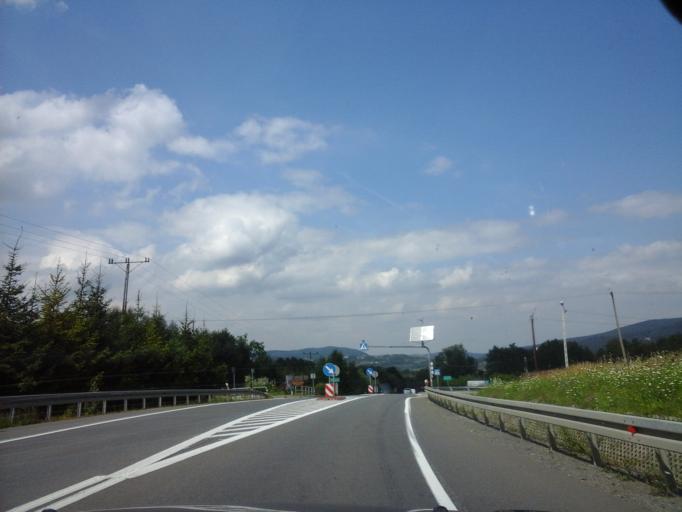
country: PL
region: Lesser Poland Voivodeship
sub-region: Powiat suski
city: Zembrzyce
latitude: 49.7986
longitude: 19.5538
